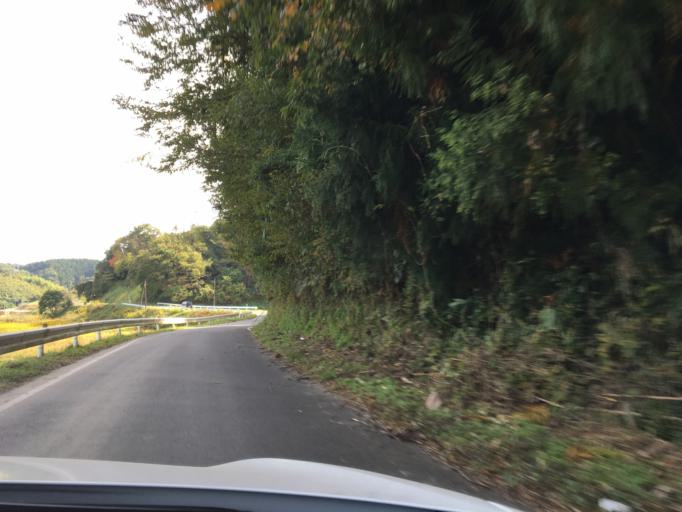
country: JP
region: Fukushima
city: Miharu
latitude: 37.5107
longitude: 140.4989
